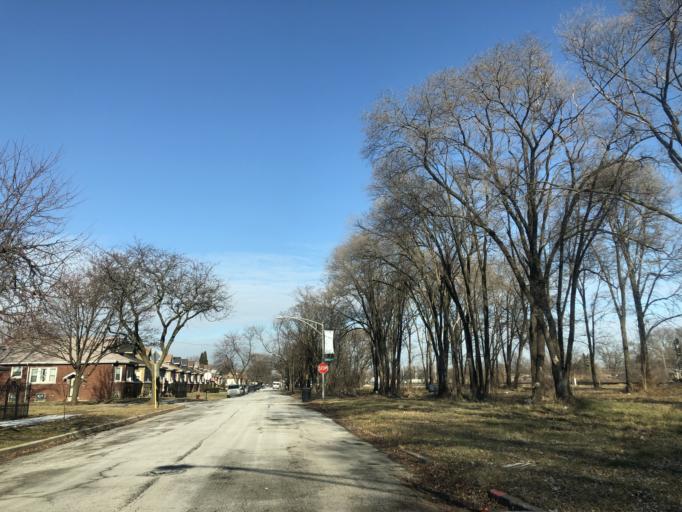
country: US
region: Illinois
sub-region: Cook County
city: Evergreen Park
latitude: 41.7606
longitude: -87.6794
